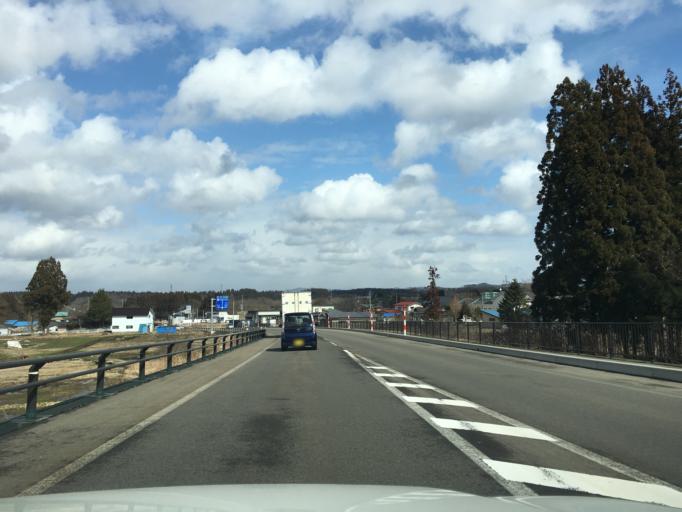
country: JP
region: Akita
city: Takanosu
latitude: 40.1173
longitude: 140.3775
